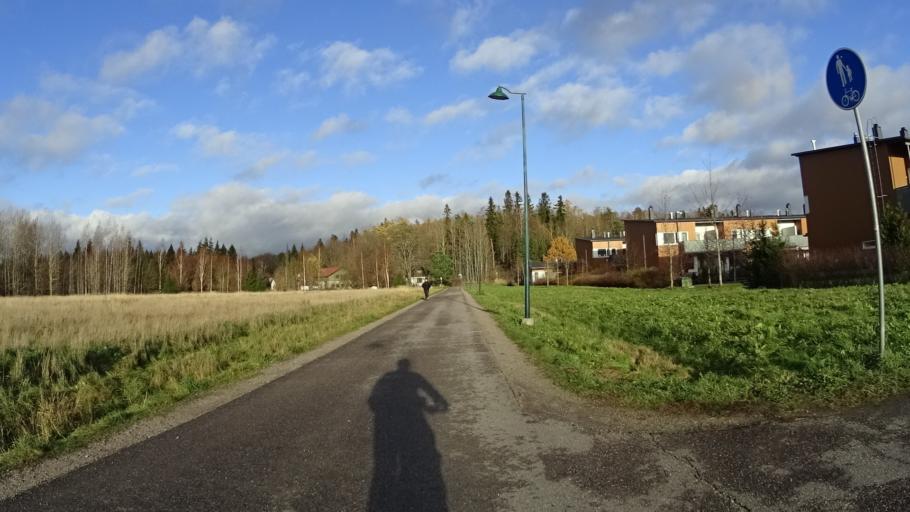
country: FI
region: Uusimaa
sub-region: Helsinki
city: Vantaa
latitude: 60.2740
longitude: 24.9577
